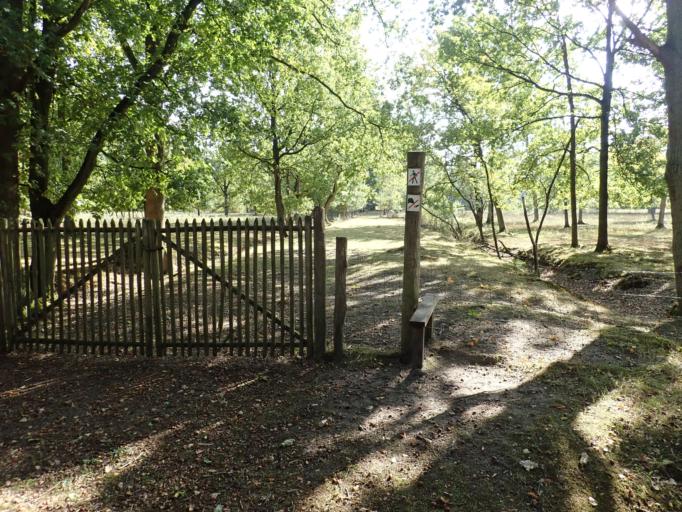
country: NL
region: Zeeland
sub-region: Gemeente Hulst
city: Hulst
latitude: 51.2458
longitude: 4.0723
